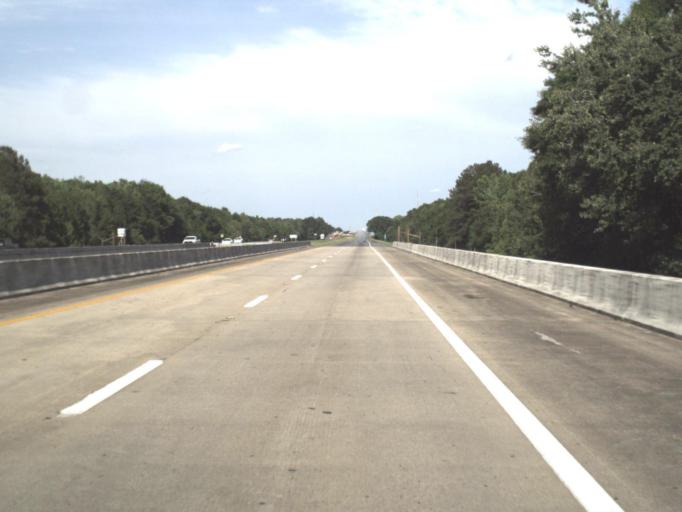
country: US
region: Florida
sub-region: Holmes County
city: Bonifay
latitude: 30.7535
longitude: -85.8439
